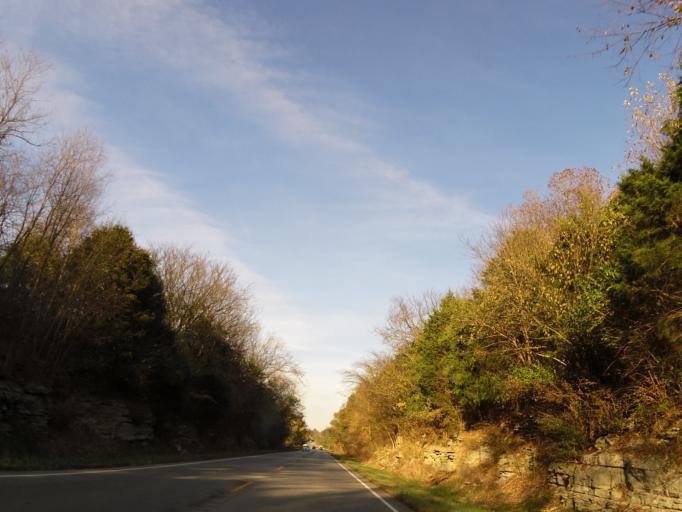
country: US
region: Kentucky
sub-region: Lincoln County
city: Stanford
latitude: 37.5651
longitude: -84.6218
